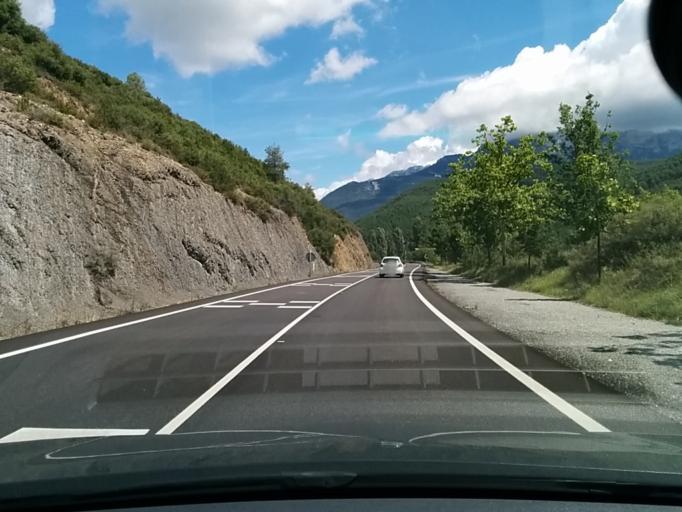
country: ES
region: Aragon
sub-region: Provincia de Huesca
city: Labuerda
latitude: 42.4533
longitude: 0.1349
